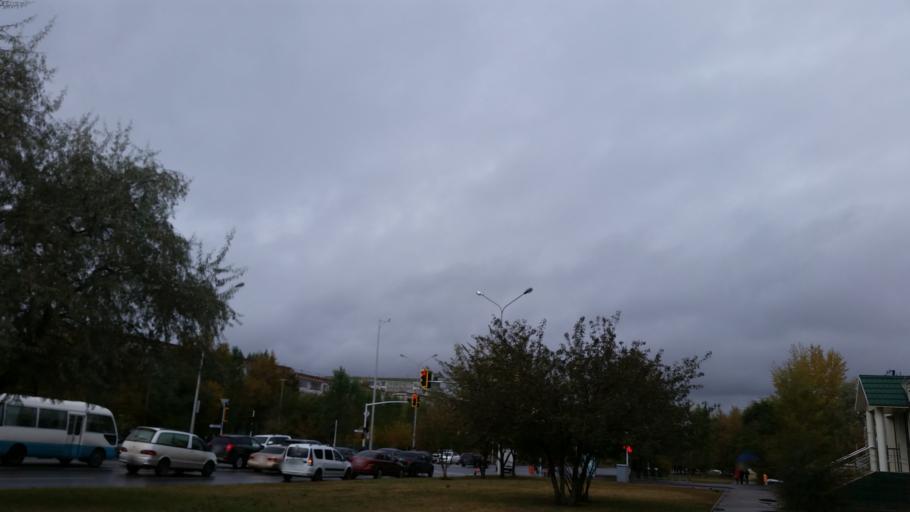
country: KZ
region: Astana Qalasy
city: Astana
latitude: 51.1514
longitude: 71.4817
